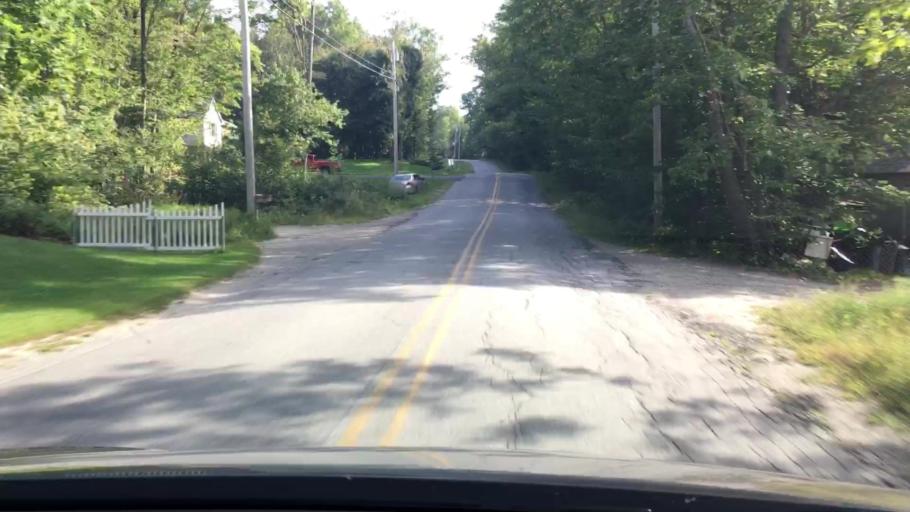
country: US
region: Maine
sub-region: Hancock County
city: Bucksport
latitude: 44.5520
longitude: -68.7963
